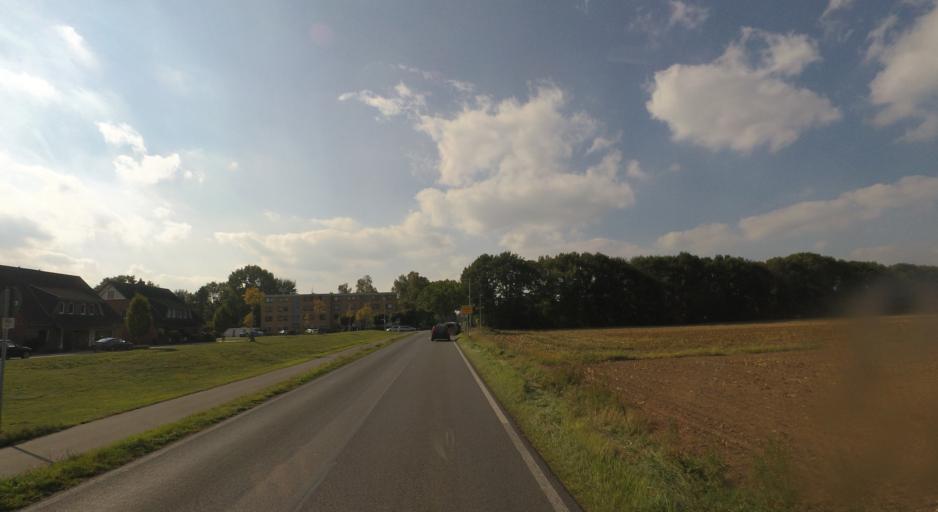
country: DE
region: North Rhine-Westphalia
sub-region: Regierungsbezirk Dusseldorf
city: Wesel
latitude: 51.6705
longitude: 6.6557
